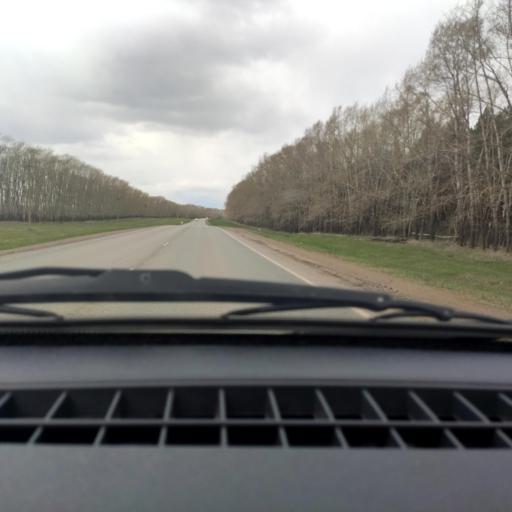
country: RU
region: Bashkortostan
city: Kushnarenkovo
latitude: 55.0866
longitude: 55.3537
